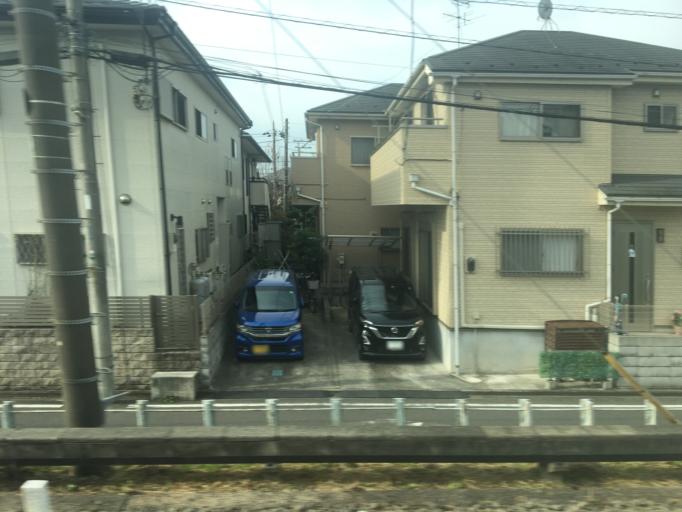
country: JP
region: Saitama
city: Sayama
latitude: 35.8356
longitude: 139.4242
